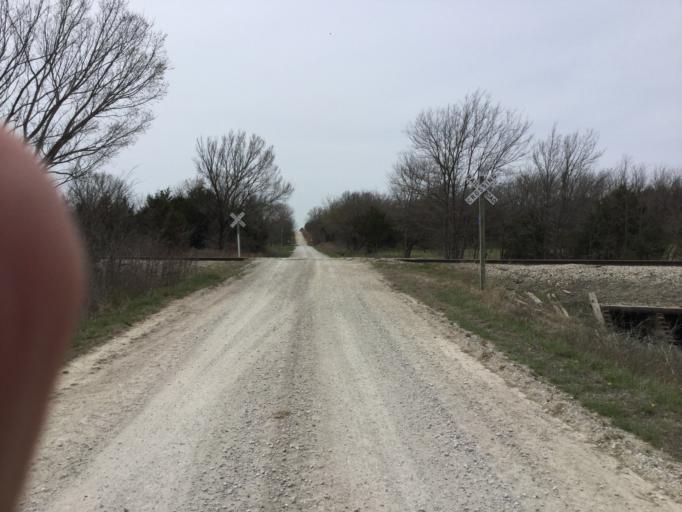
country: US
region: Kansas
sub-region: Wilson County
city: Fredonia
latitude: 37.4723
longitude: -95.8790
